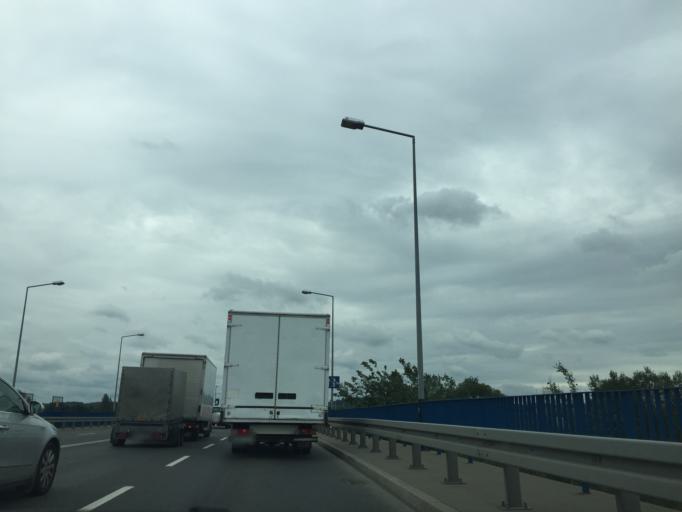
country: PL
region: Lesser Poland Voivodeship
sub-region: Powiat krakowski
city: Libertow
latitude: 49.9934
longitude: 19.9177
